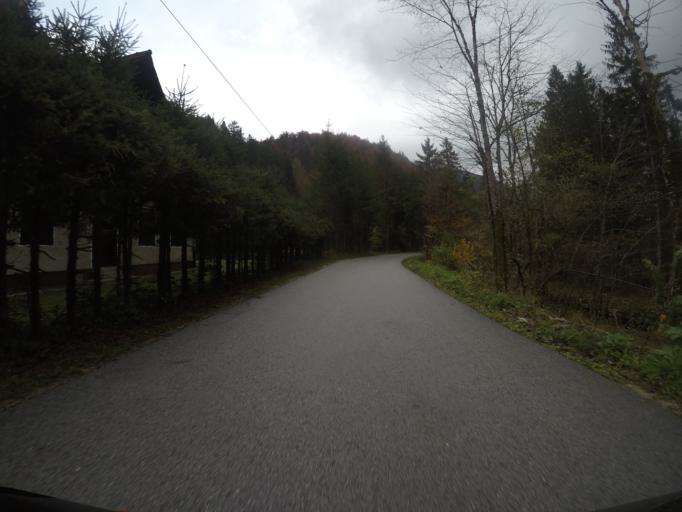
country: SI
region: Jesenice
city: Hrusica
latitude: 46.4091
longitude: 13.9969
